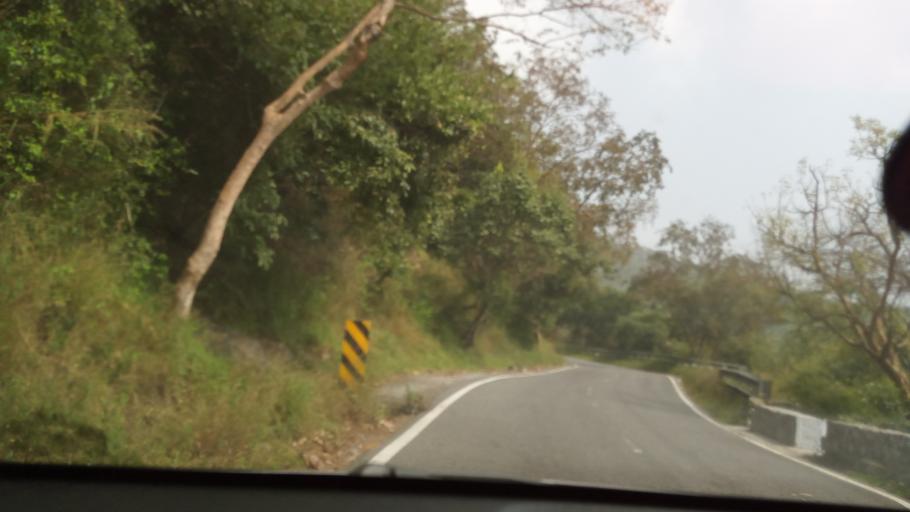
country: IN
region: Tamil Nadu
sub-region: Erode
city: Sathyamangalam
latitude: 11.5997
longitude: 77.1254
